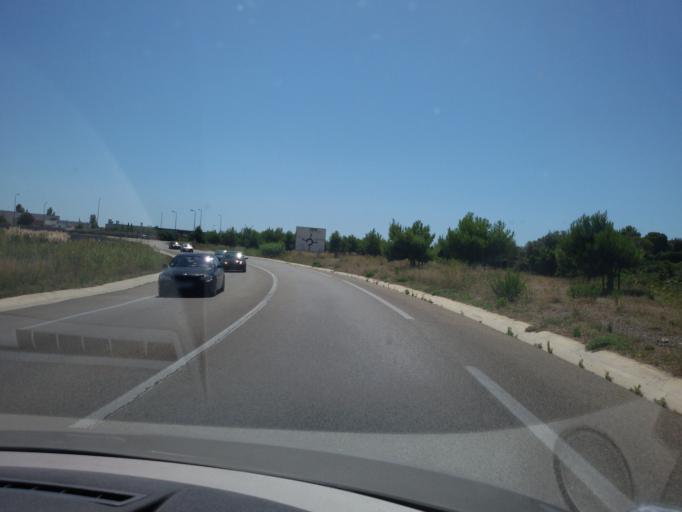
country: FR
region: Languedoc-Roussillon
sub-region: Departement de l'Herault
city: Frontignan
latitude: 43.4681
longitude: 3.7659
